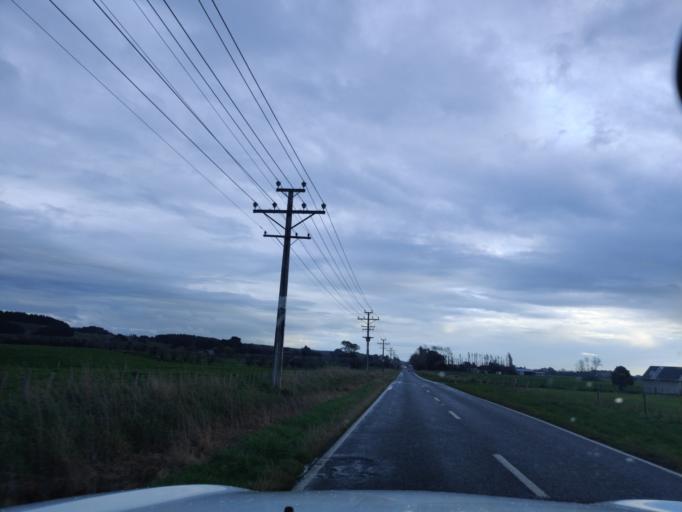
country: NZ
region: Manawatu-Wanganui
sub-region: Palmerston North City
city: Palmerston North
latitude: -40.3458
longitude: 175.7078
